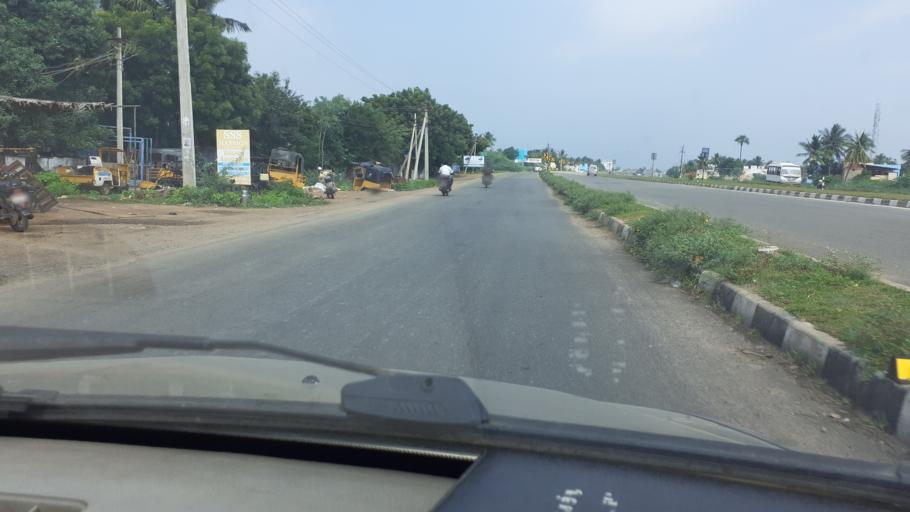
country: IN
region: Tamil Nadu
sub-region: Tirunelveli Kattabo
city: Tirunelveli
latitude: 8.7066
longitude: 77.7655
